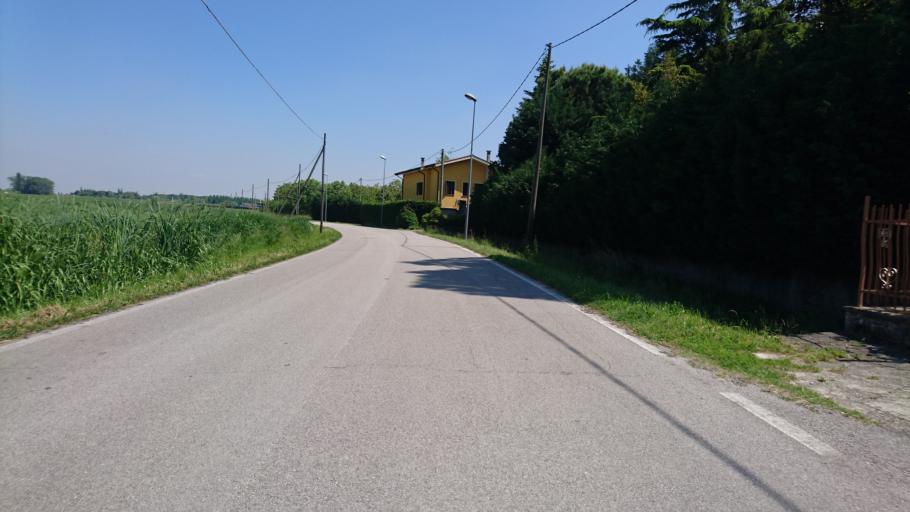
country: IT
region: Veneto
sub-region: Provincia di Padova
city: Casalserugo
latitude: 45.2965
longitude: 11.9167
